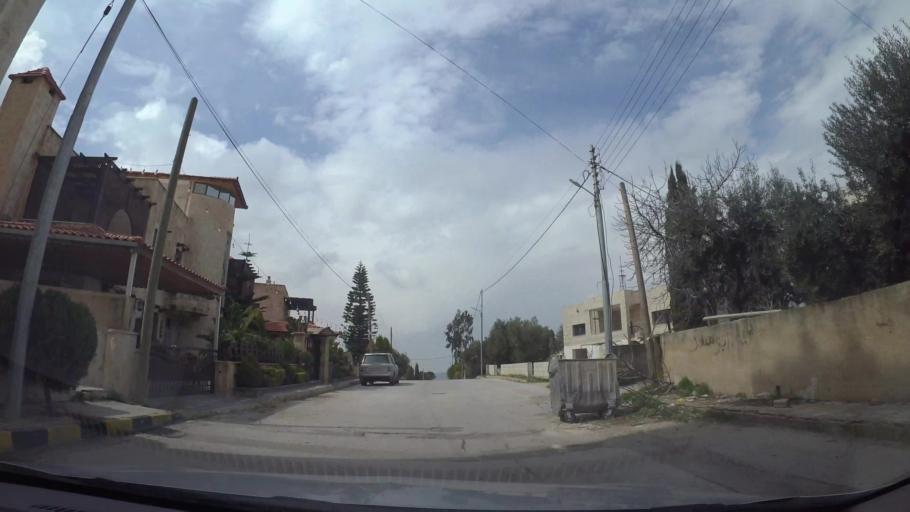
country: JO
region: Amman
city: Umm as Summaq
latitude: 31.8972
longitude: 35.8365
